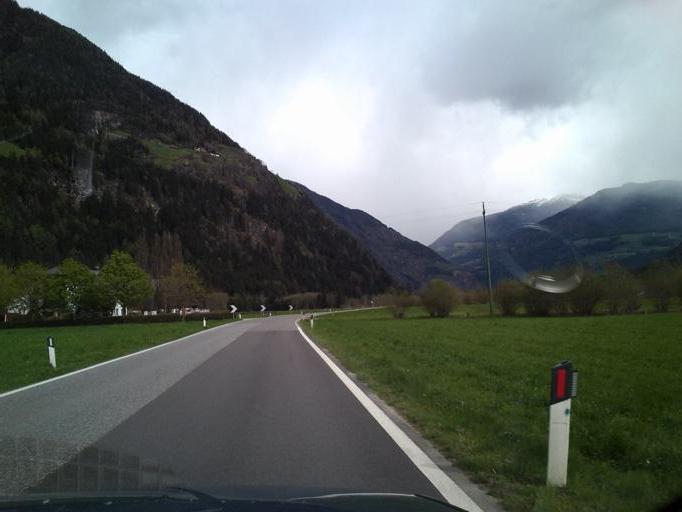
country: IT
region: Trentino-Alto Adige
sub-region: Bolzano
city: Molini di Tures
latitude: 46.8711
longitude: 11.9486
